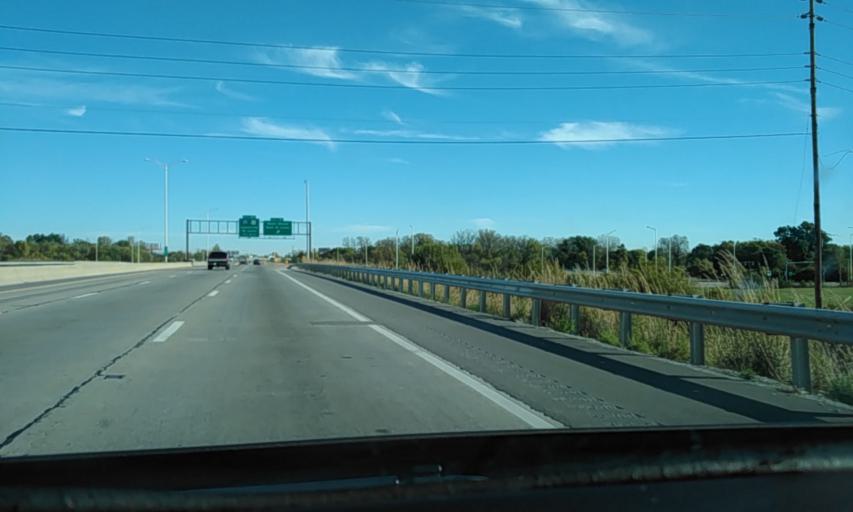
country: US
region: Illinois
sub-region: Saint Clair County
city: Washington Park
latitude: 38.6010
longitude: -90.0863
